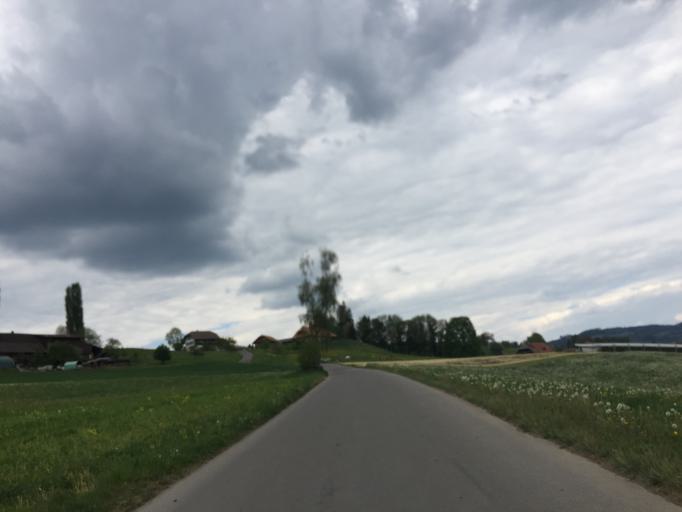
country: CH
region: Bern
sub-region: Thun District
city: Seftigen
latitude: 46.8010
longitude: 7.5521
